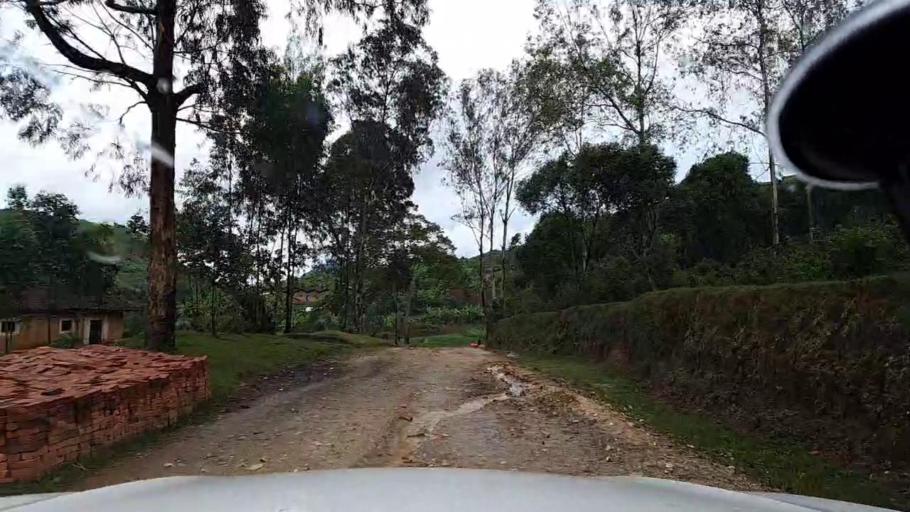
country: RW
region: Western Province
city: Kibuye
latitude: -2.1194
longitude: 29.4932
